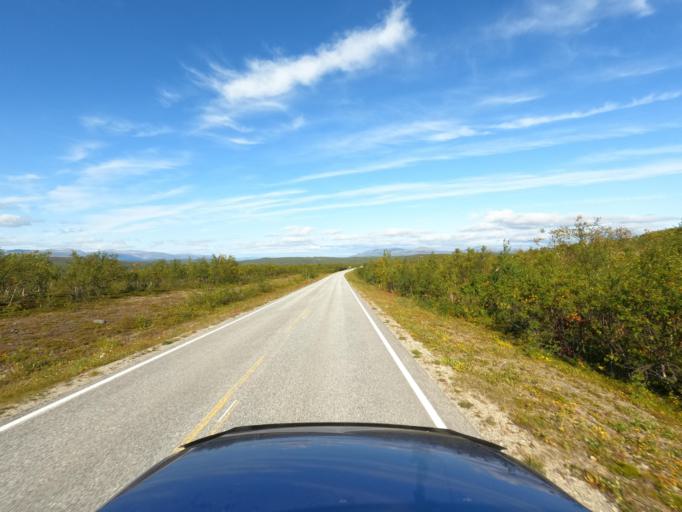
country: NO
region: Finnmark Fylke
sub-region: Karasjok
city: Karasjohka
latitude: 69.7252
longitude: 25.2356
